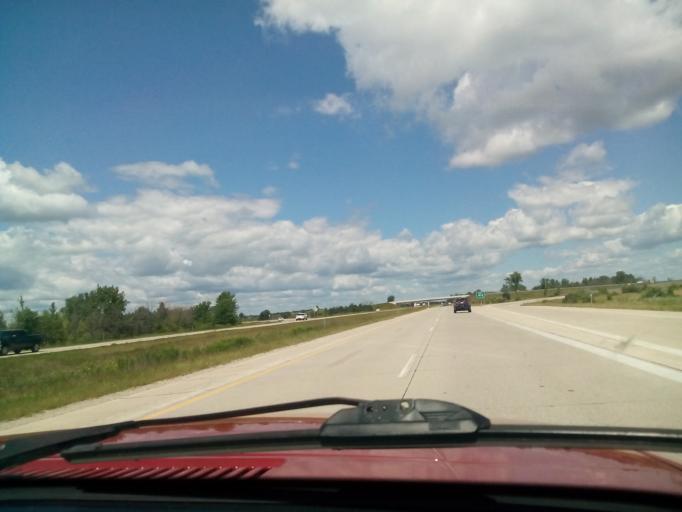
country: US
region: Michigan
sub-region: Bay County
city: Pinconning
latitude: 43.8485
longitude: -84.0204
